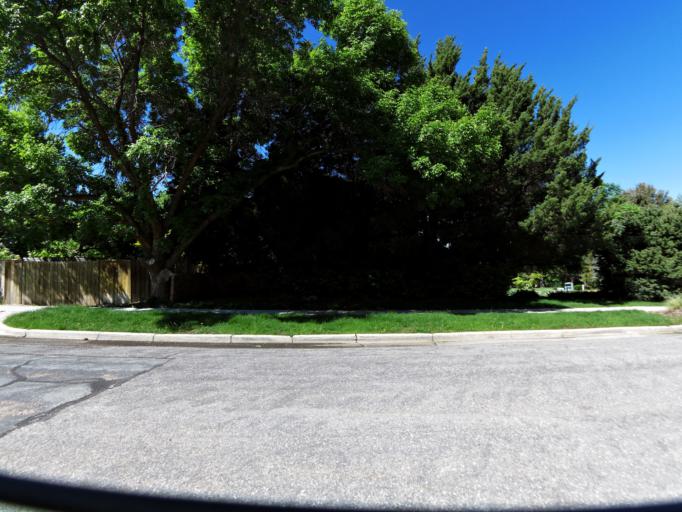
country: US
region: Utah
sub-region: Weber County
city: Uintah
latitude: 41.1708
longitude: -111.9309
